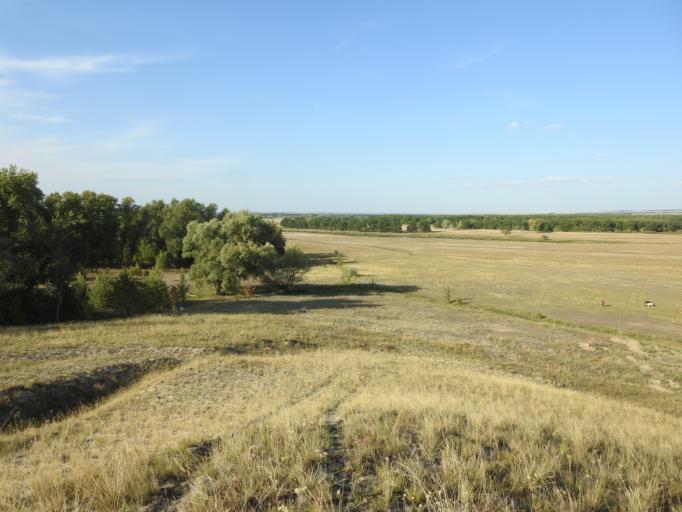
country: RU
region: Volgograd
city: Zhirnovsk
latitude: 51.1910
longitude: 44.9443
